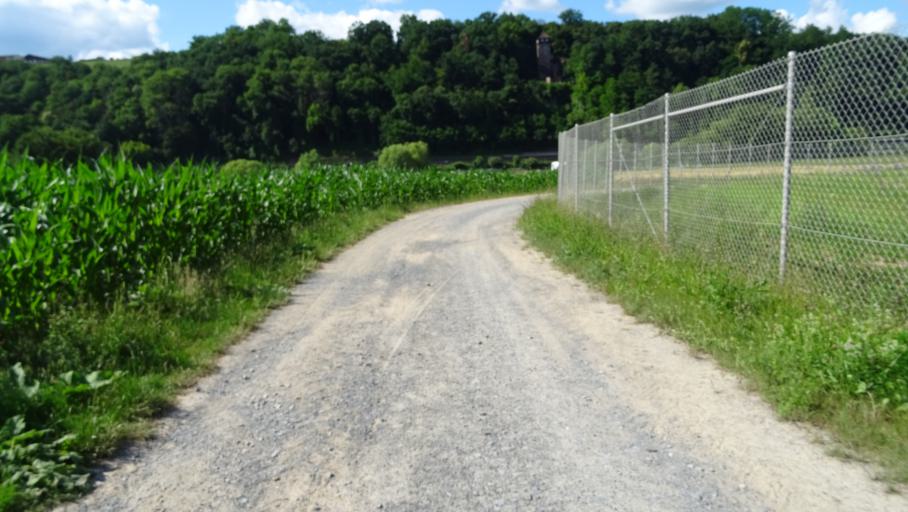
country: DE
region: Baden-Wuerttemberg
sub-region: Karlsruhe Region
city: Binau
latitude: 49.3658
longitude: 9.0733
